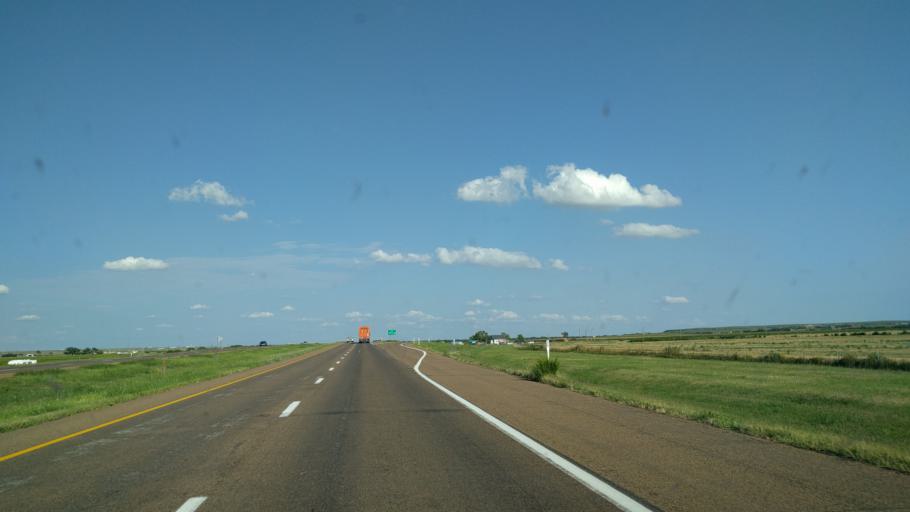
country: US
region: Kansas
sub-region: Ellis County
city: Hays
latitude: 38.9241
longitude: -99.4326
